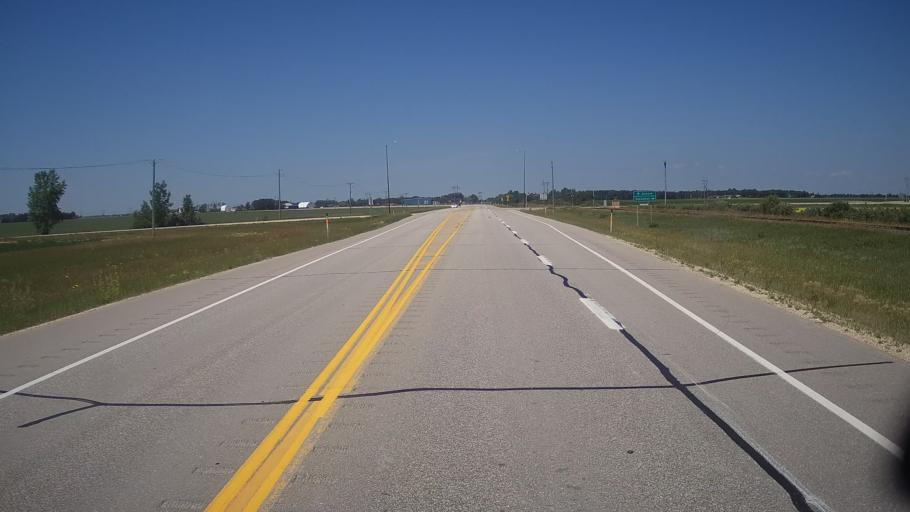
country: CA
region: Manitoba
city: Stonewall
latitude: 50.1191
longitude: -97.5266
